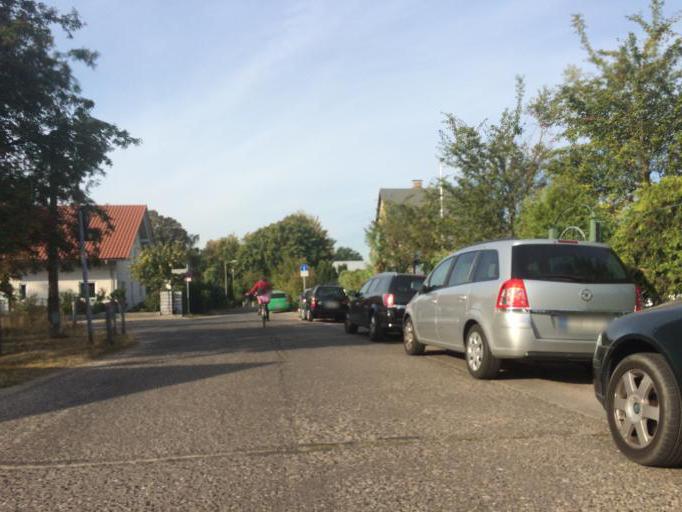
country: DE
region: Berlin
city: Alt-Hohenschoenhausen
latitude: 52.5581
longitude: 13.4956
